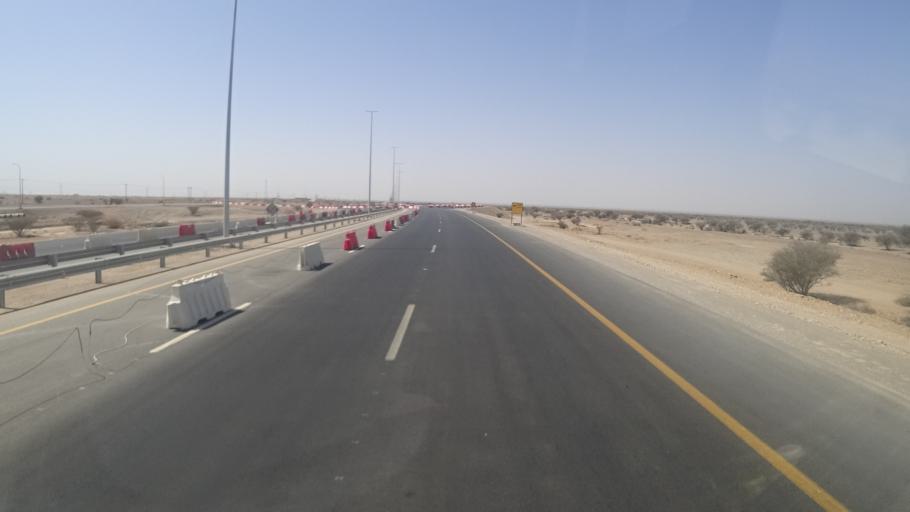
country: OM
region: Ash Sharqiyah
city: Sur
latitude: 22.3137
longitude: 59.2913
